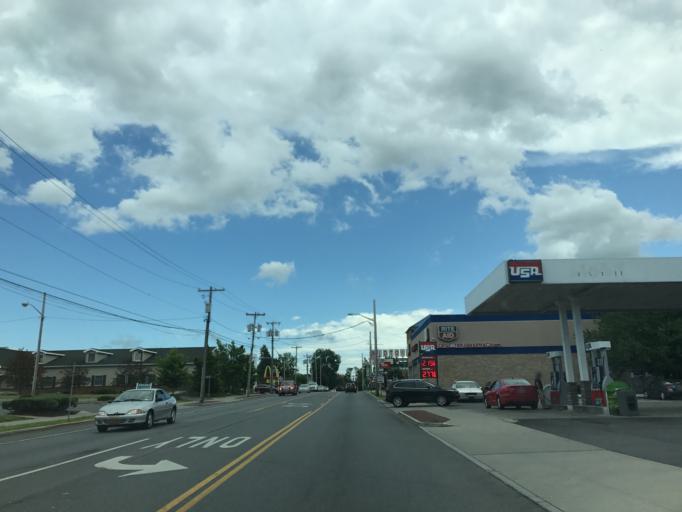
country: US
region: New York
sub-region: Saratoga County
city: South Glens Falls
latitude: 43.3010
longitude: -73.6370
